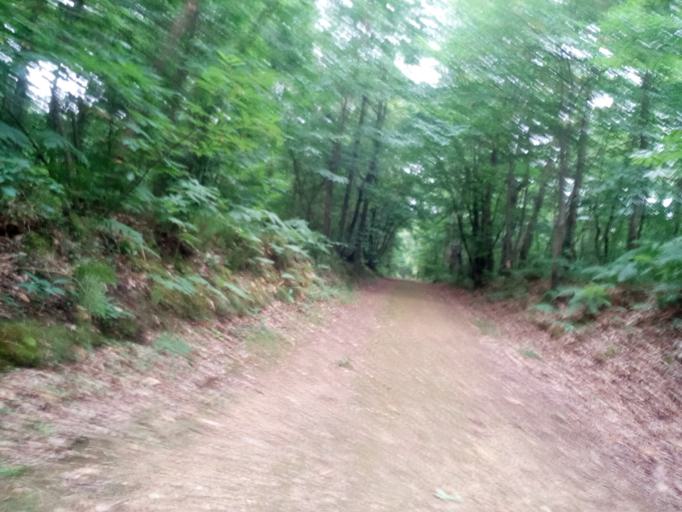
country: FR
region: Lower Normandy
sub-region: Departement du Calvados
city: Clinchamps-sur-Orne
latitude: 49.0400
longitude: -0.4367
